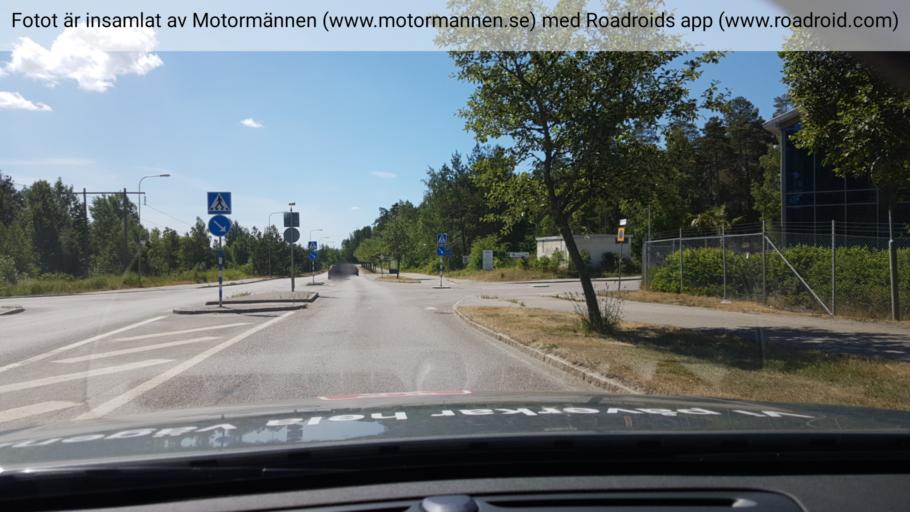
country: SE
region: Stockholm
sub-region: Nacka Kommun
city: Alta
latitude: 59.2376
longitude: 18.1948
